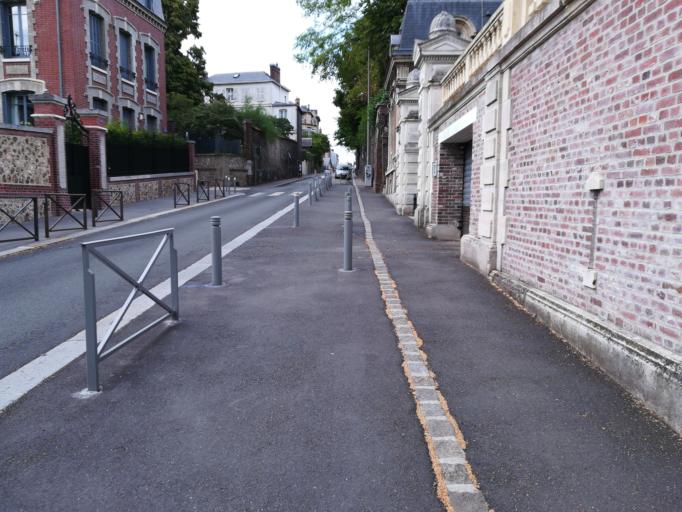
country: FR
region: Haute-Normandie
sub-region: Departement de la Seine-Maritime
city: Rouen
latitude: 49.4510
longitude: 1.0930
